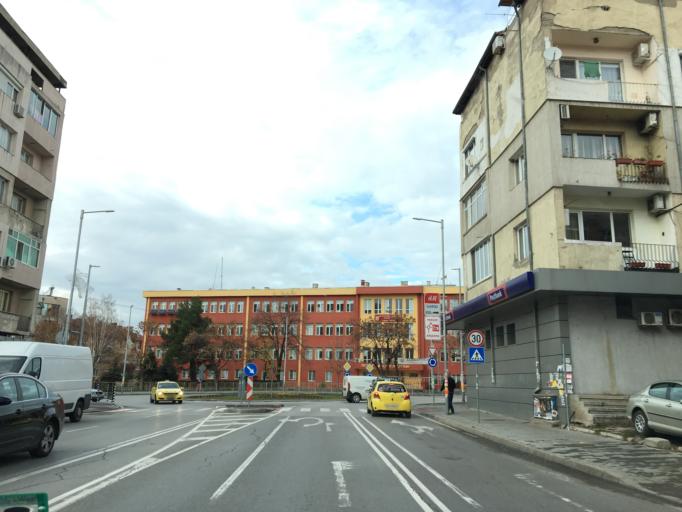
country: BG
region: Blagoevgrad
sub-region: Obshtina Blagoevgrad
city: Blagoevgrad
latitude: 42.0165
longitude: 23.0949
